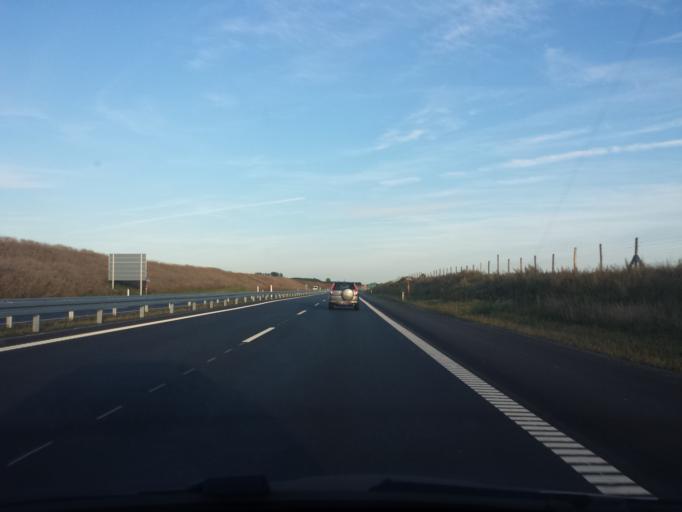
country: DK
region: Capital Region
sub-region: Ballerup Kommune
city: Ballerup
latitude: 55.7127
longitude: 12.3344
